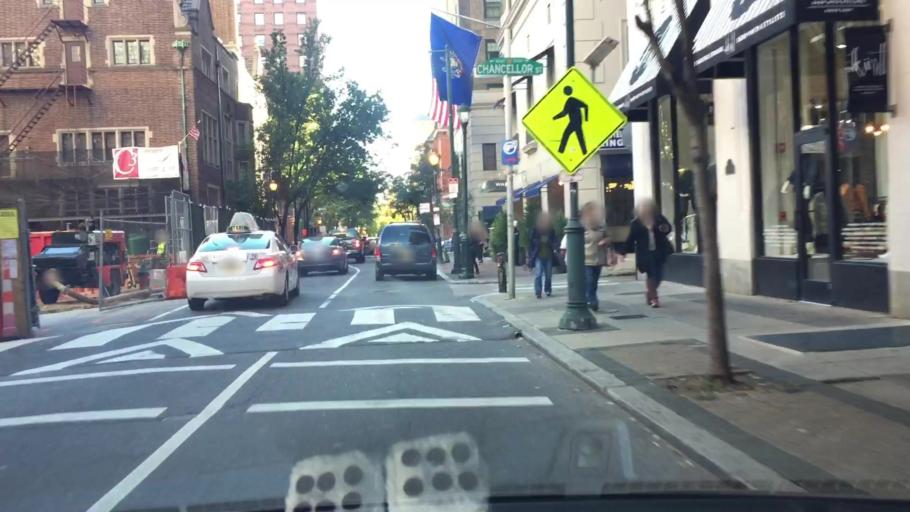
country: US
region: Pennsylvania
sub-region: Philadelphia County
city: Philadelphia
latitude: 39.9496
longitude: -75.1691
